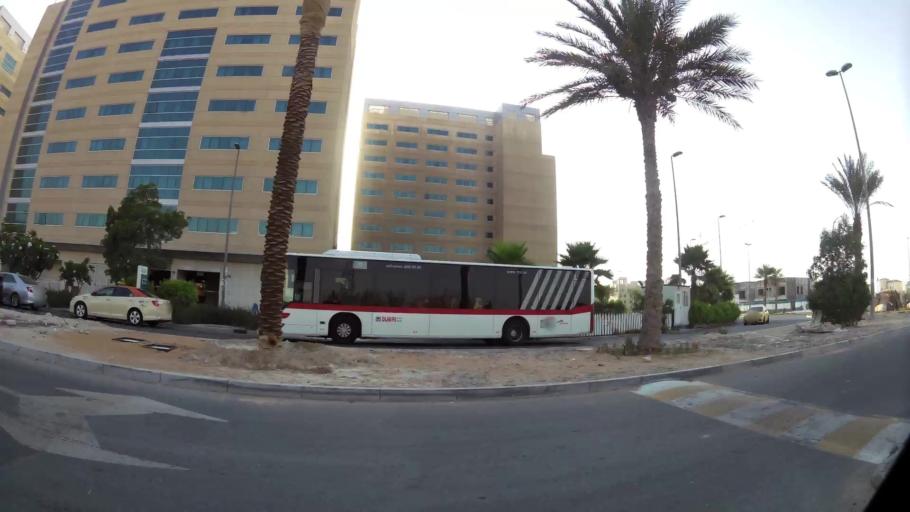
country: AE
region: Dubai
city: Dubai
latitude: 25.0676
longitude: 55.2105
